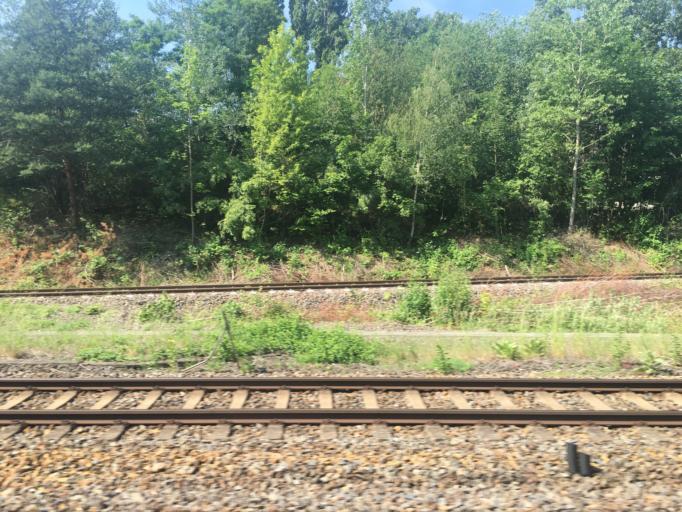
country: DE
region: Berlin
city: Friedrichshain Bezirk
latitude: 52.5343
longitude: 13.4497
